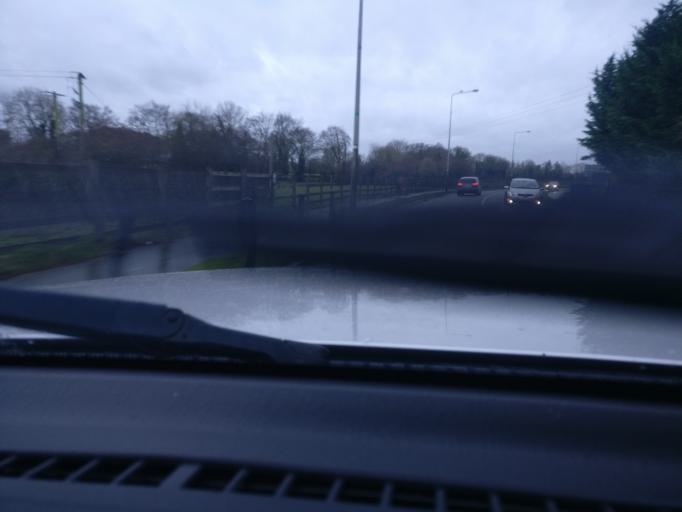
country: IE
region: Leinster
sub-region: An Mhi
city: Trim
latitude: 53.5466
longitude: -6.7947
